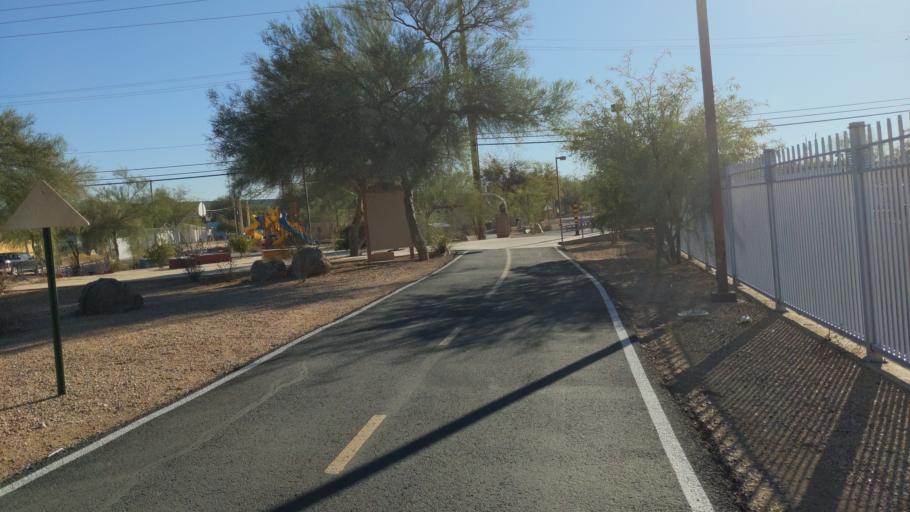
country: US
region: Arizona
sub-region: Pima County
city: South Tucson
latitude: 32.1891
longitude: -110.9764
